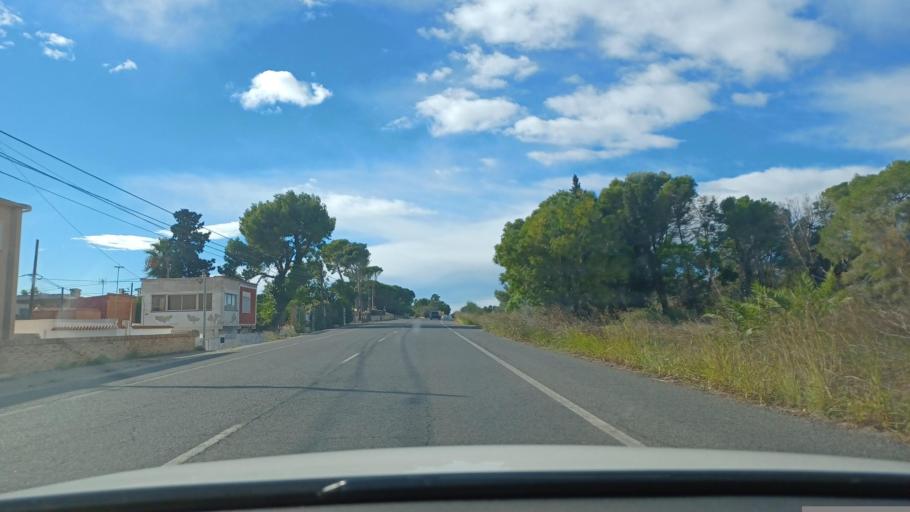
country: ES
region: Catalonia
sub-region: Provincia de Tarragona
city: Sant Carles de la Rapita
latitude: 40.6034
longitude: 0.5793
